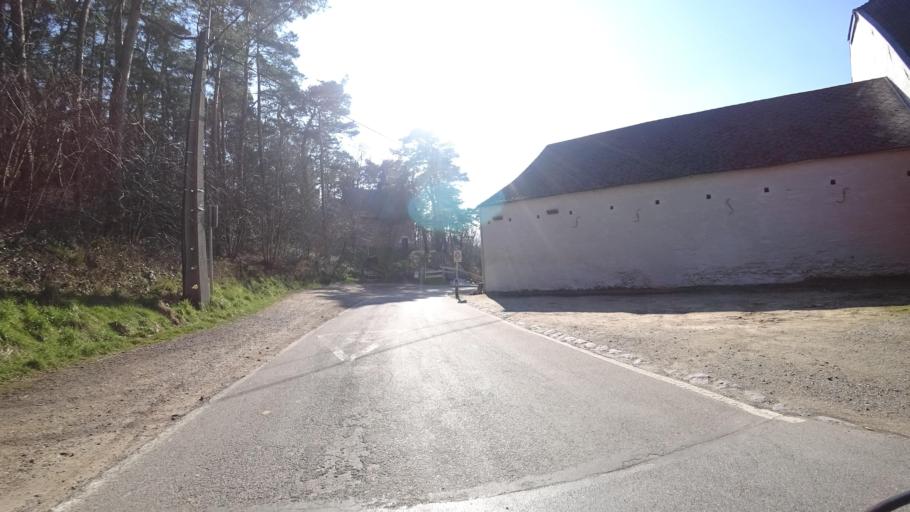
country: BE
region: Wallonia
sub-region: Province du Brabant Wallon
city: Court-Saint-Etienne
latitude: 50.6203
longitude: 4.5643
